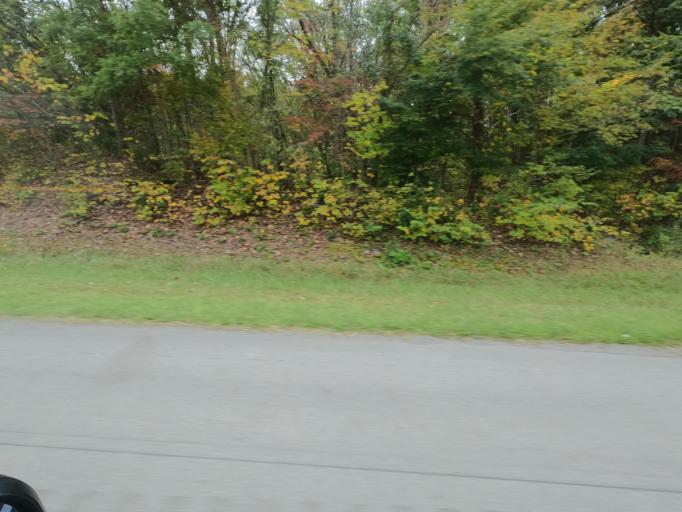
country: US
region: Tennessee
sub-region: Sullivan County
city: Kingsport
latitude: 36.5147
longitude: -82.5752
